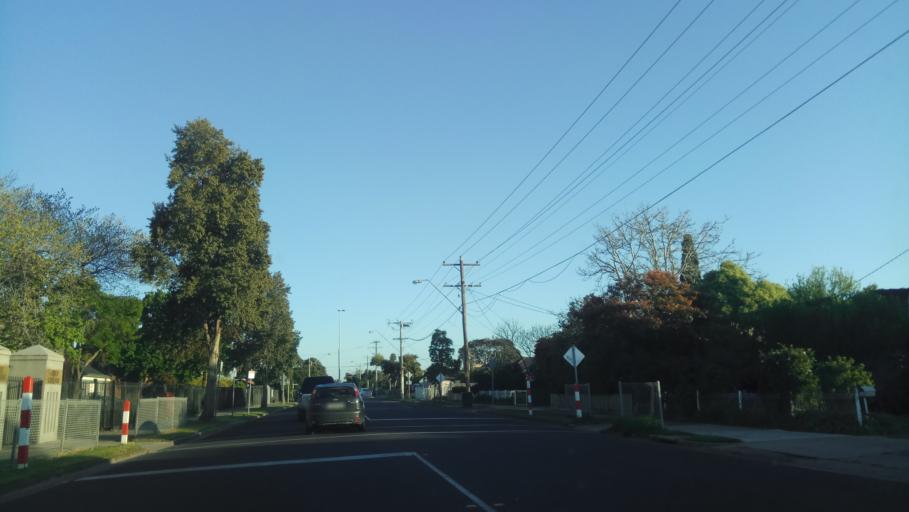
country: AU
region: Victoria
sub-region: Hobsons Bay
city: Altona
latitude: -37.8643
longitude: 144.8125
